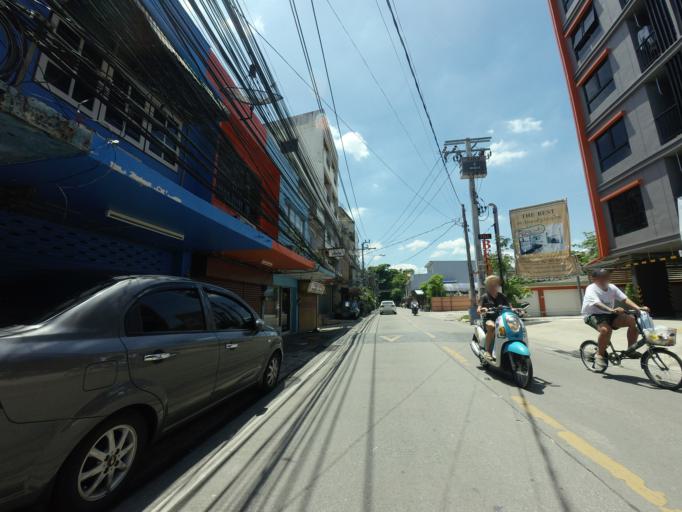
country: TH
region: Bangkok
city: Huai Khwang
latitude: 13.7969
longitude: 100.5859
